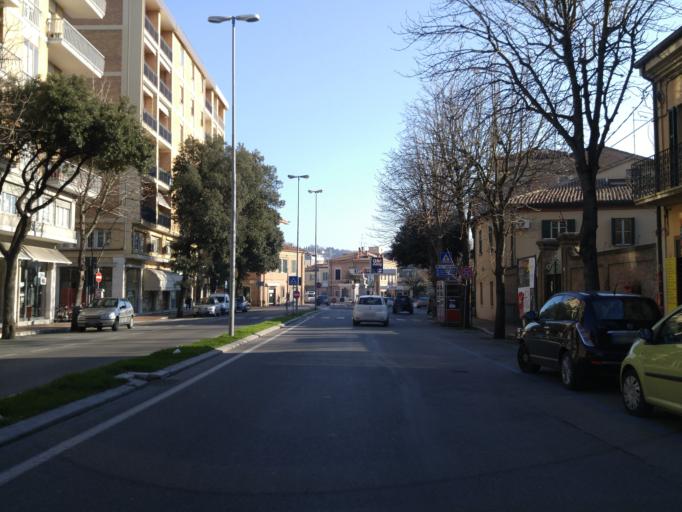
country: IT
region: The Marches
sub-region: Provincia di Pesaro e Urbino
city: Pesaro
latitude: 43.9080
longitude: 12.9162
